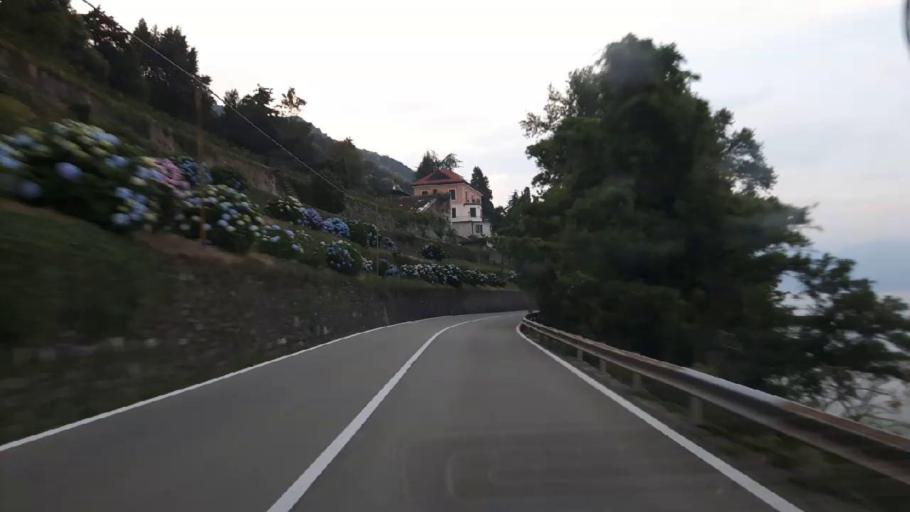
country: IT
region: Piedmont
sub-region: Provincia Verbano-Cusio-Ossola
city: Belgirate
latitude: 45.8502
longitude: 8.5702
